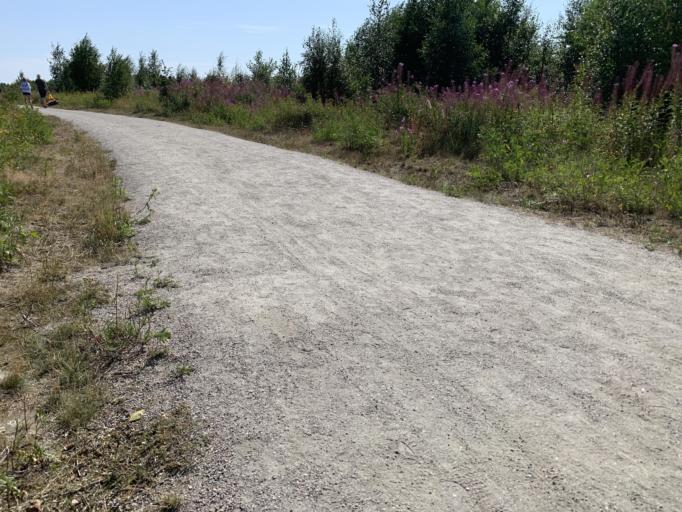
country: SE
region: Vaesternorrland
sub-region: Timra Kommun
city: Soraker
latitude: 62.5149
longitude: 17.4498
